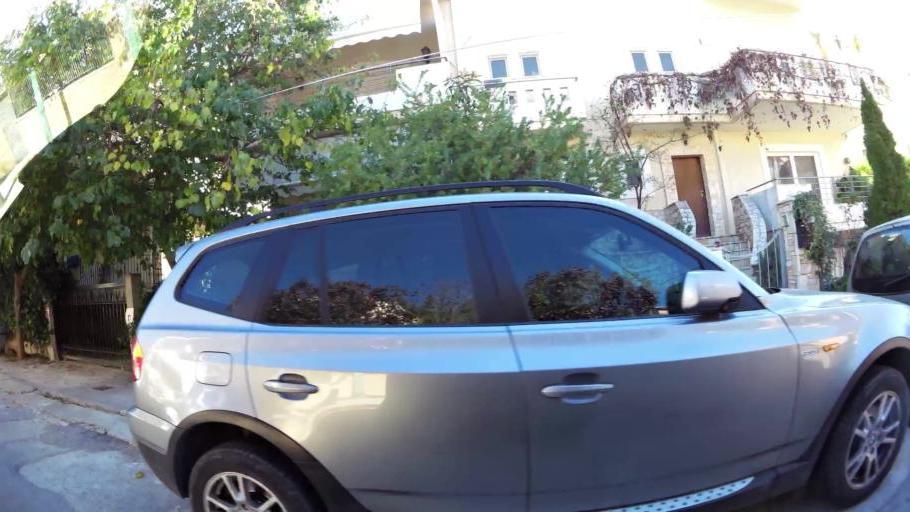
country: GR
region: Attica
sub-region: Nomarchia Athinas
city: Vrilissia
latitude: 38.0261
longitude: 23.8351
